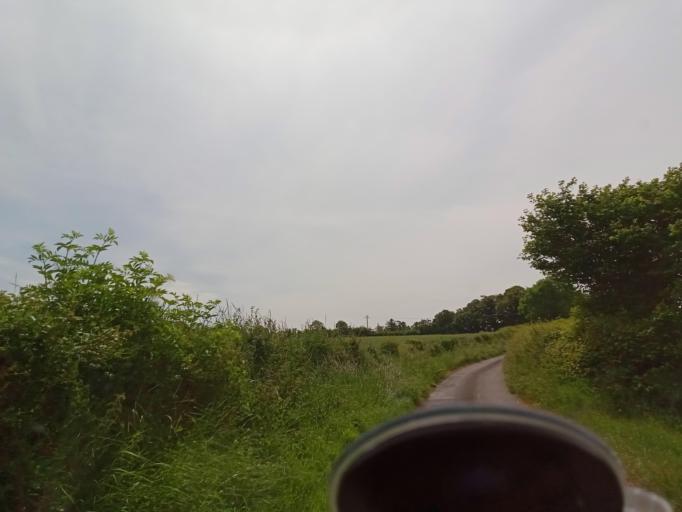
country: IE
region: Leinster
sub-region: Kilkenny
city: Thomastown
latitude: 52.5620
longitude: -7.1036
